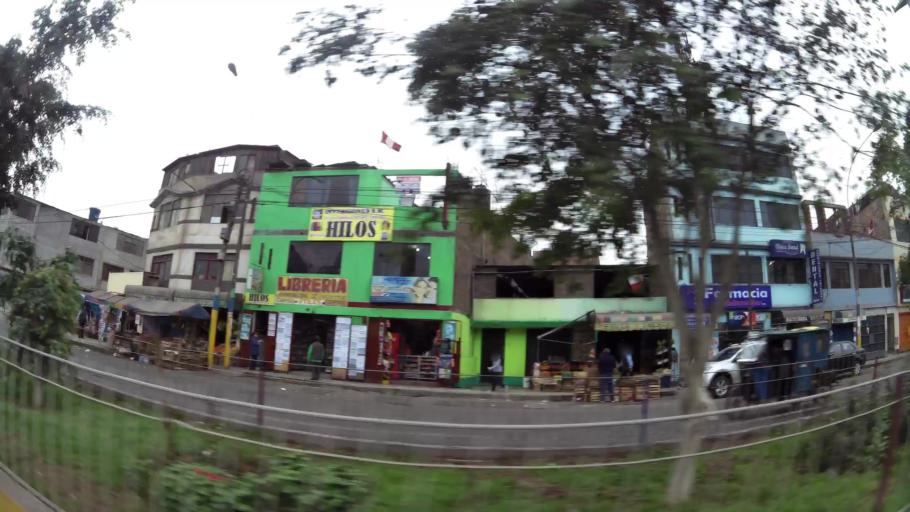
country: PE
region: Lima
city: Lima
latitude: -12.0127
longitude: -77.0082
